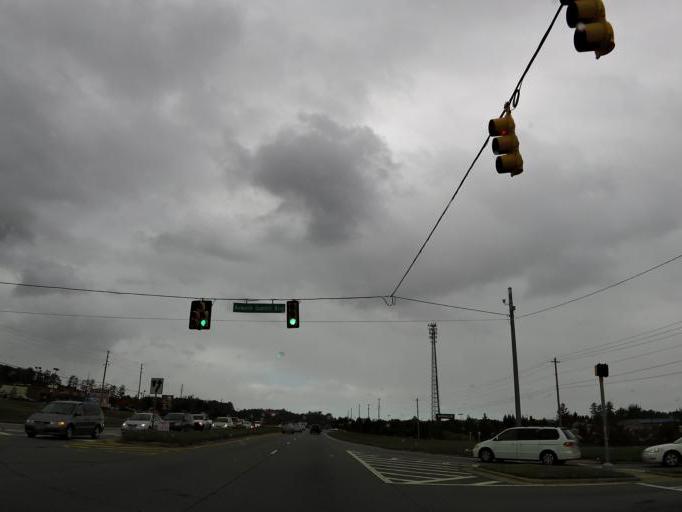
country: US
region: Georgia
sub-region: Cobb County
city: Acworth
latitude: 34.0352
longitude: -84.6798
